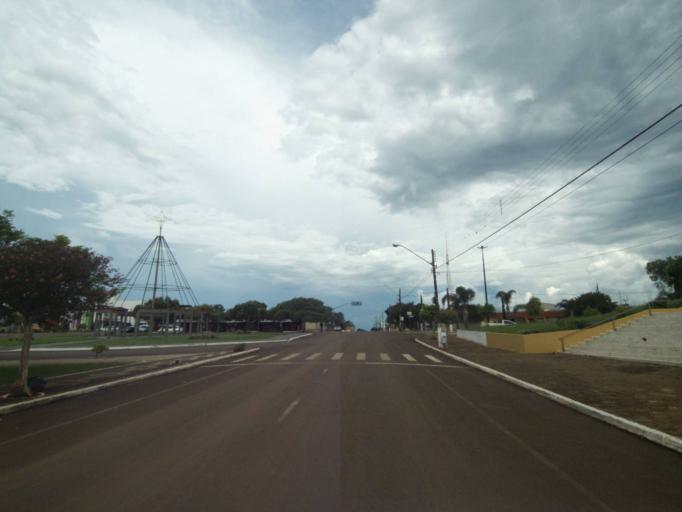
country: BR
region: Parana
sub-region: Guaraniacu
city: Guaraniacu
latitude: -25.1015
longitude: -52.8679
